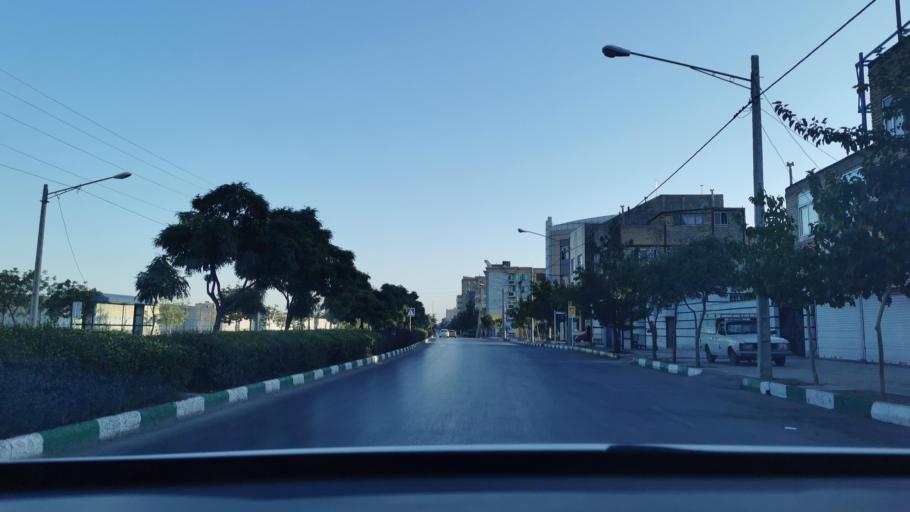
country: IR
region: Razavi Khorasan
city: Mashhad
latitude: 36.3466
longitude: 59.5142
